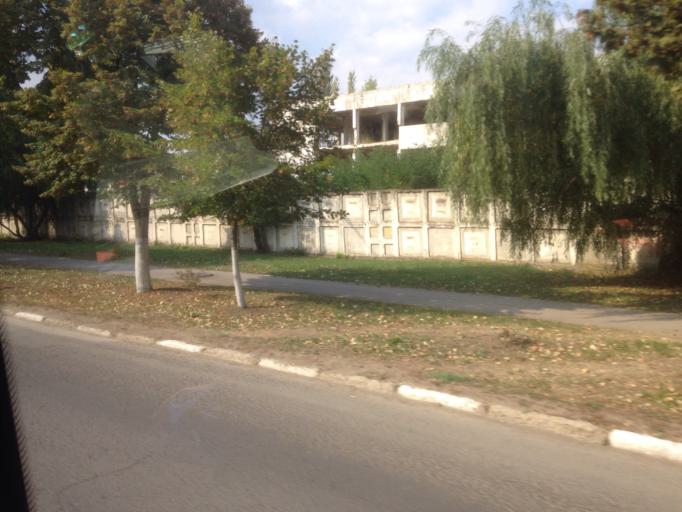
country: MD
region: Balti
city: Balti
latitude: 47.7594
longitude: 27.9407
